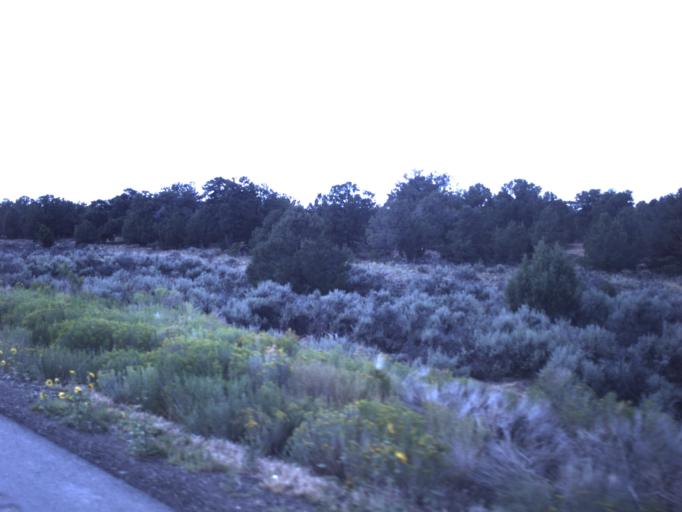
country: US
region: Utah
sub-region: Duchesne County
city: Duchesne
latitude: 40.1809
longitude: -110.6291
